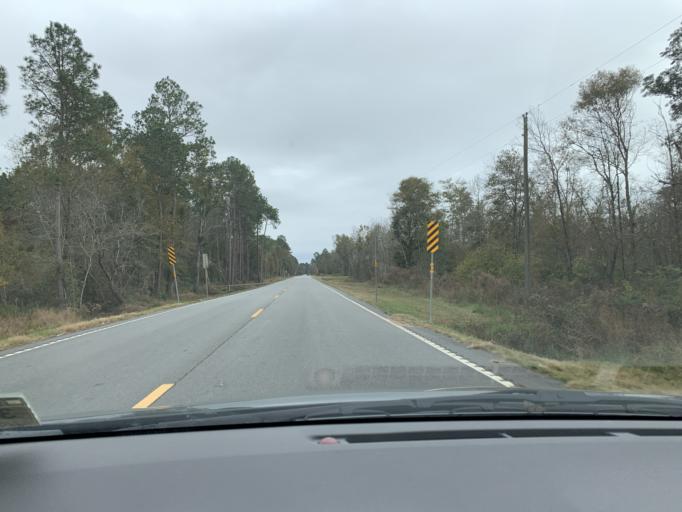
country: US
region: Georgia
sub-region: Thomas County
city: Meigs
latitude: 31.0174
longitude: -83.9599
